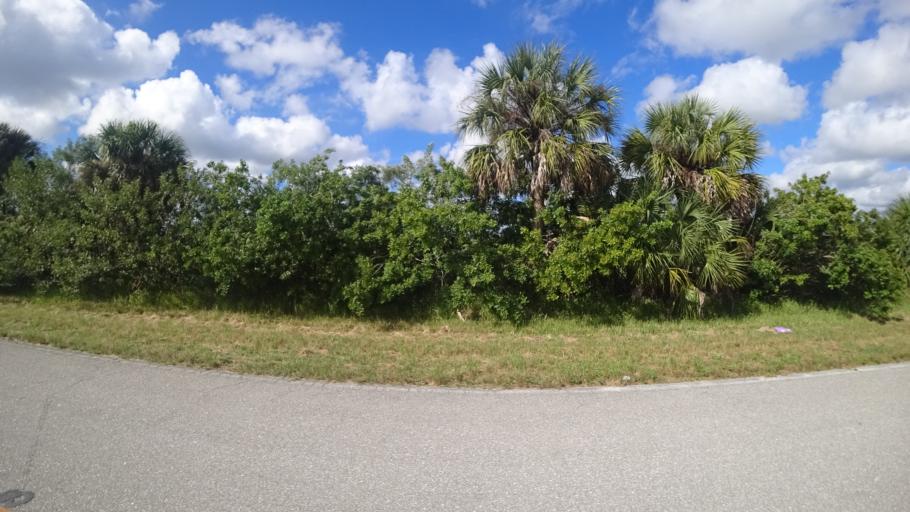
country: US
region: Florida
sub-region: Manatee County
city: Ellenton
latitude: 27.6111
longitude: -82.4818
